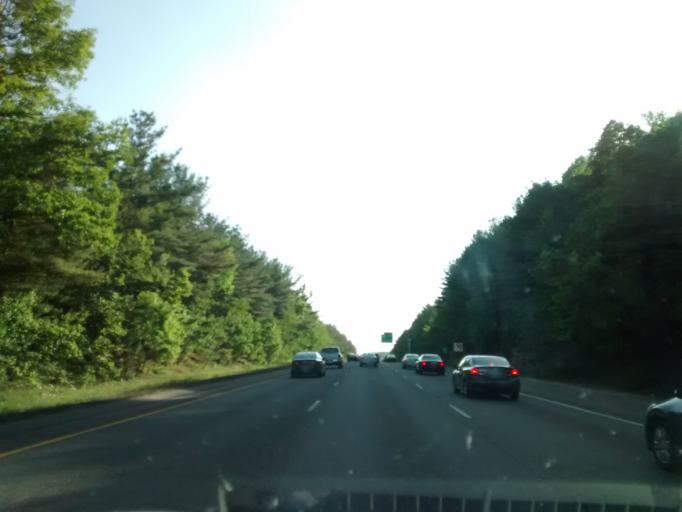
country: US
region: Massachusetts
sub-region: Worcester County
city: Shrewsbury
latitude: 42.3260
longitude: -71.7048
